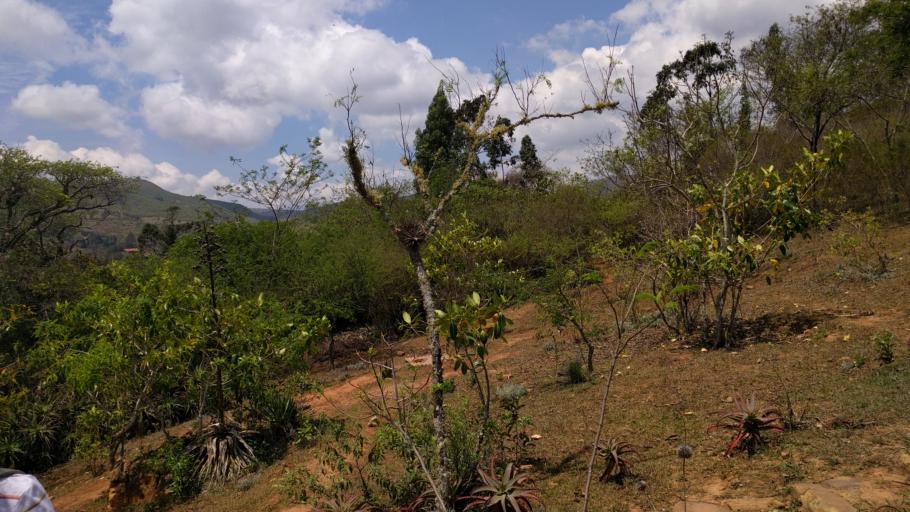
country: BO
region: Santa Cruz
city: Samaipata
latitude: -18.1883
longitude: -63.8811
